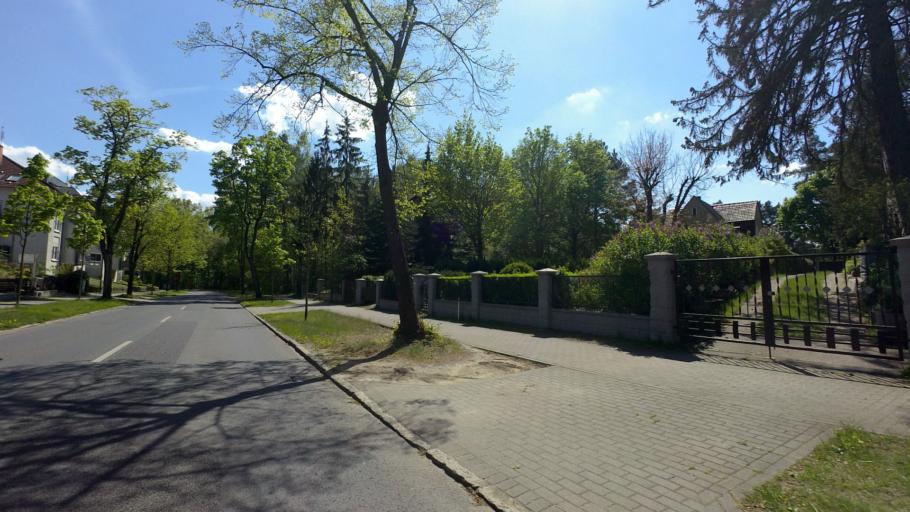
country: DE
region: Berlin
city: Lubars
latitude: 52.6382
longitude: 13.3659
